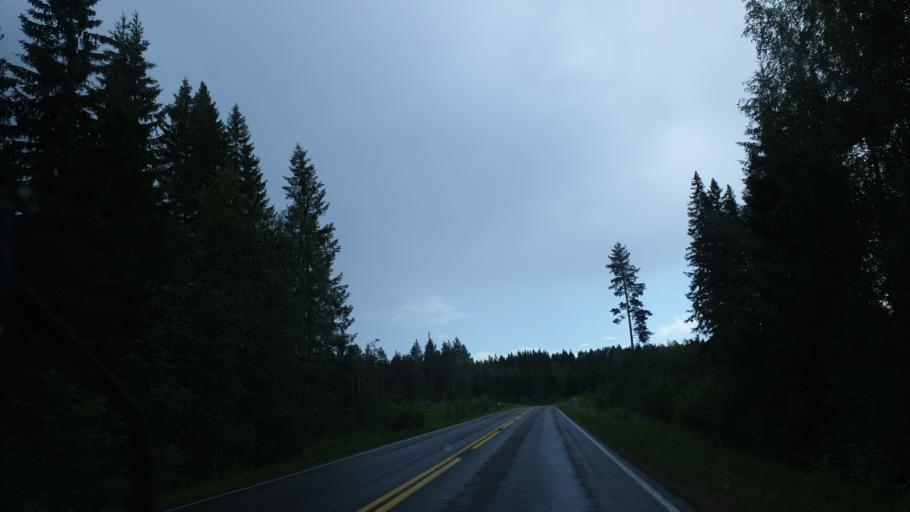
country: FI
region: Northern Savo
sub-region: Kuopio
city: Vehmersalmi
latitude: 62.9350
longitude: 27.9128
